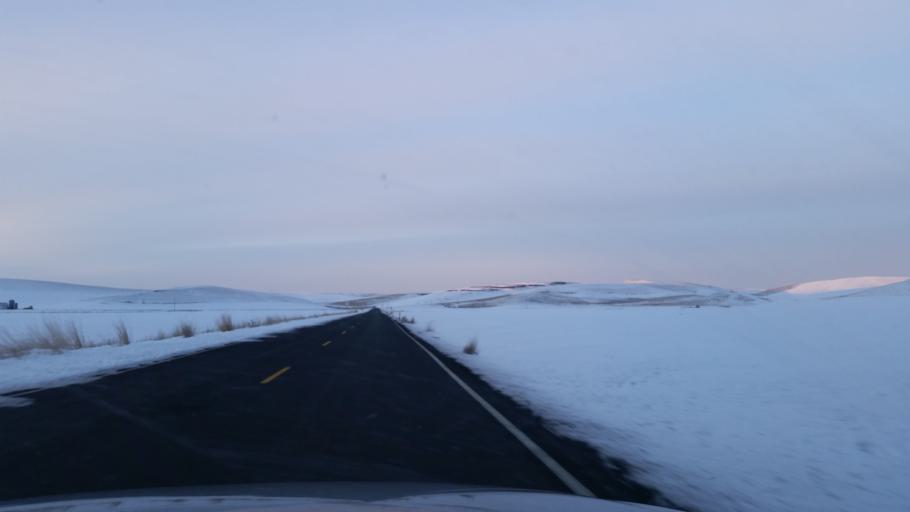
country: US
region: Washington
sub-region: Spokane County
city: Cheney
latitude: 47.1793
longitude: -117.8709
